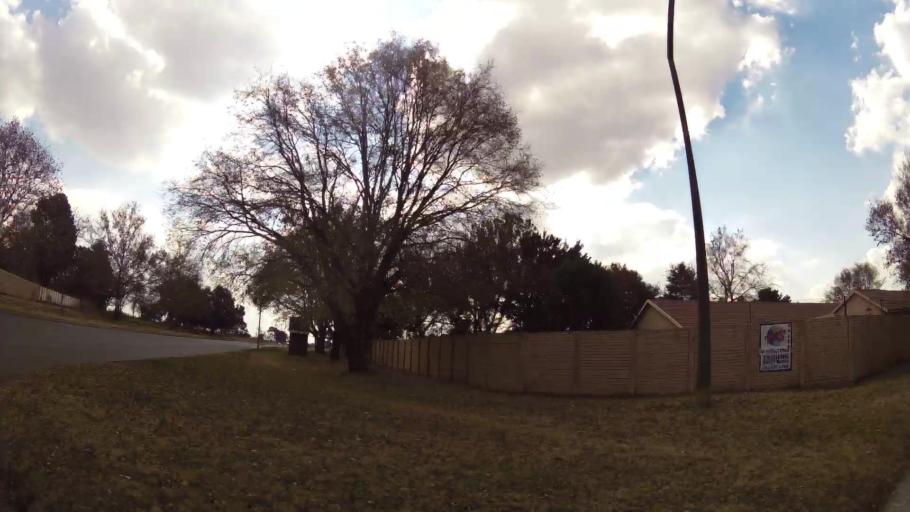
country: ZA
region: Mpumalanga
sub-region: Nkangala District Municipality
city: Delmas
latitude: -26.1423
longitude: 28.6683
